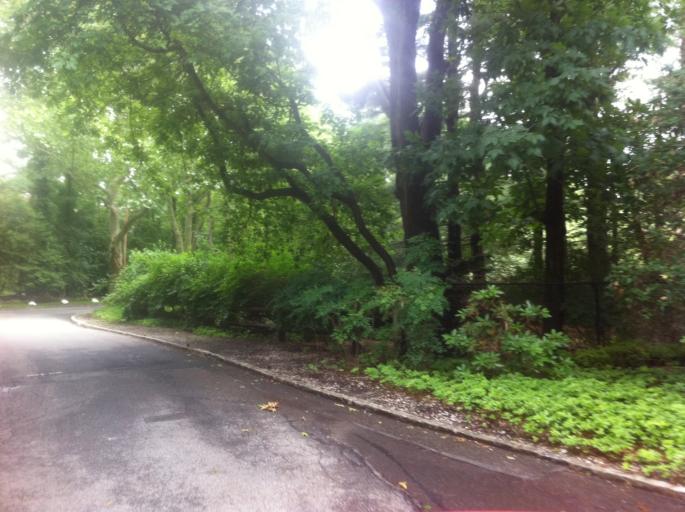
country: US
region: New York
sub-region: Nassau County
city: Bayville
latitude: 40.8881
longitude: -73.5551
